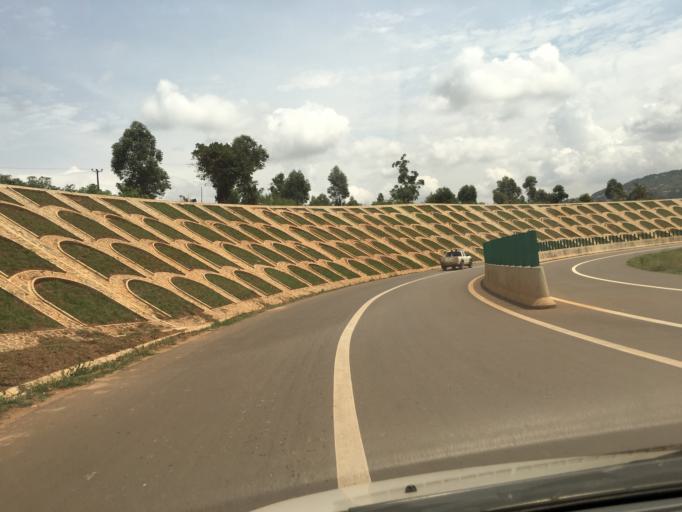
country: UG
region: Central Region
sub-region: Wakiso District
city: Kajansi
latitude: 0.2141
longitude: 32.5299
